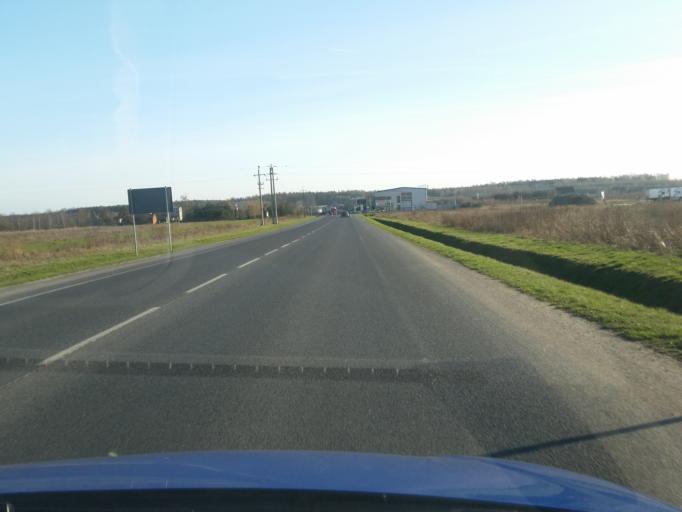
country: PL
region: Lodz Voivodeship
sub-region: Powiat radomszczanski
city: Radomsko
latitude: 51.0835
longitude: 19.3800
